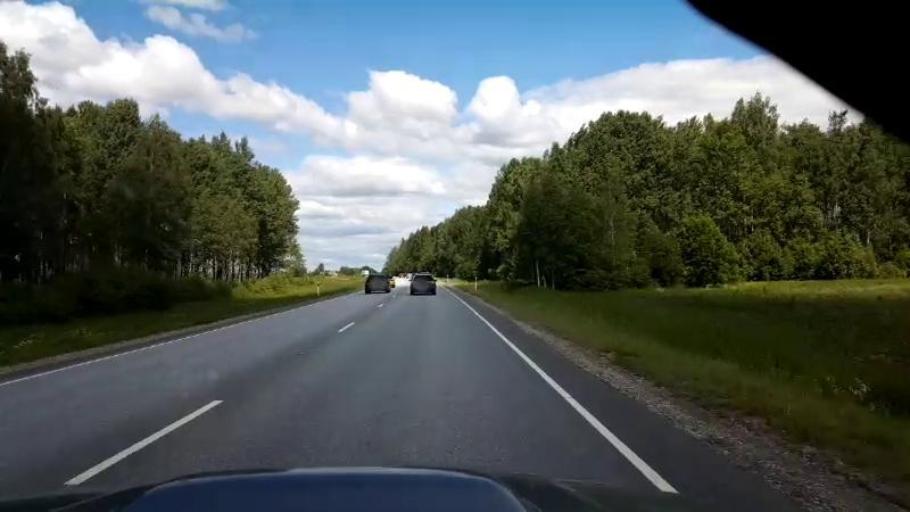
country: EE
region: Paernumaa
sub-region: Sauga vald
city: Sauga
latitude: 58.4736
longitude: 24.5267
